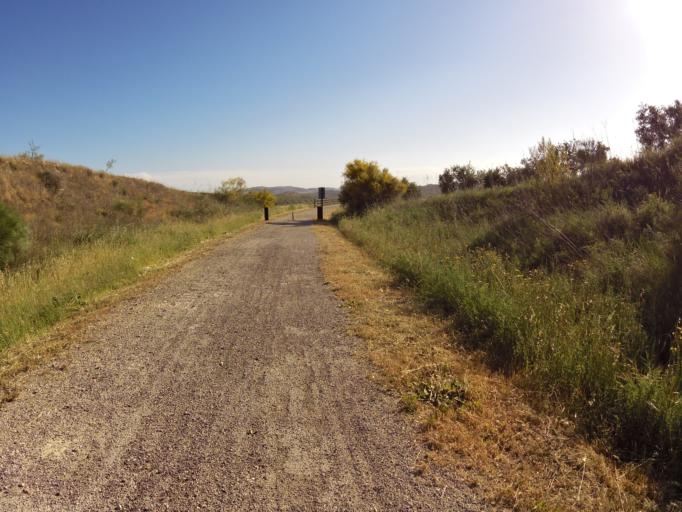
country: ES
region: Andalusia
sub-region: Province of Cordoba
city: Luque
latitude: 37.5692
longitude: -4.2349
